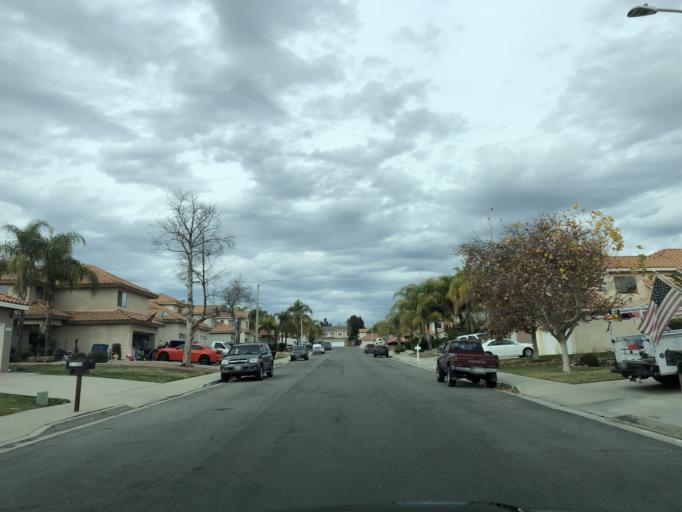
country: US
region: California
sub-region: Riverside County
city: Wildomar
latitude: 33.6071
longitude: -117.2640
